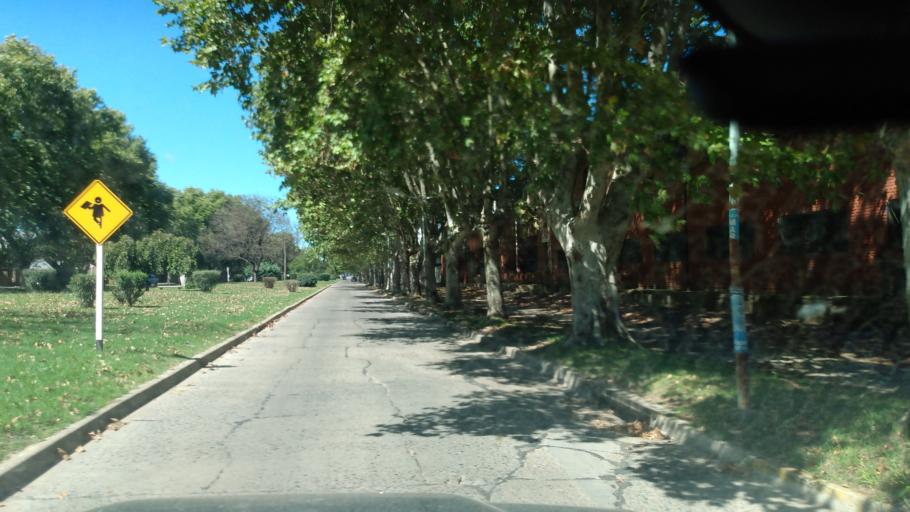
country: AR
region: Buenos Aires
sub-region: Partido de Lujan
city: Lujan
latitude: -34.5743
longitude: -59.1098
